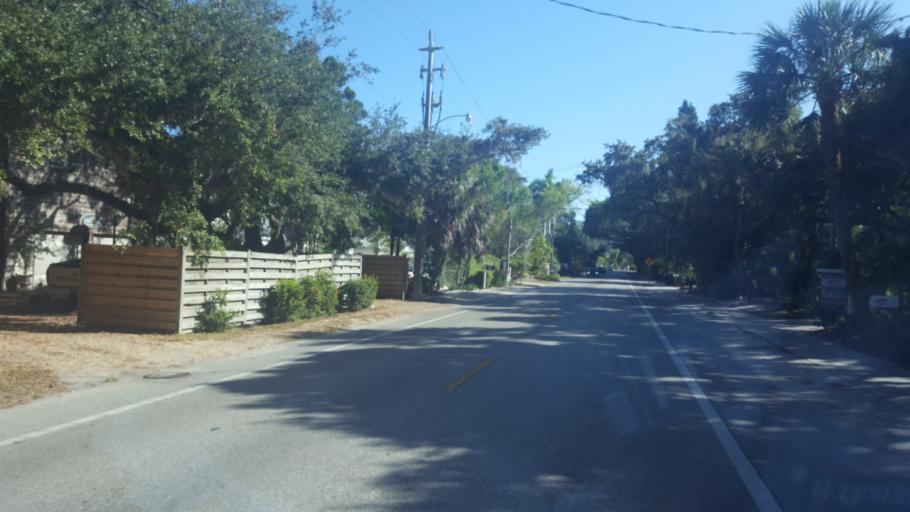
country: US
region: Florida
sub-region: Sarasota County
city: Gulf Gate Estates
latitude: 27.2349
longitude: -82.5223
